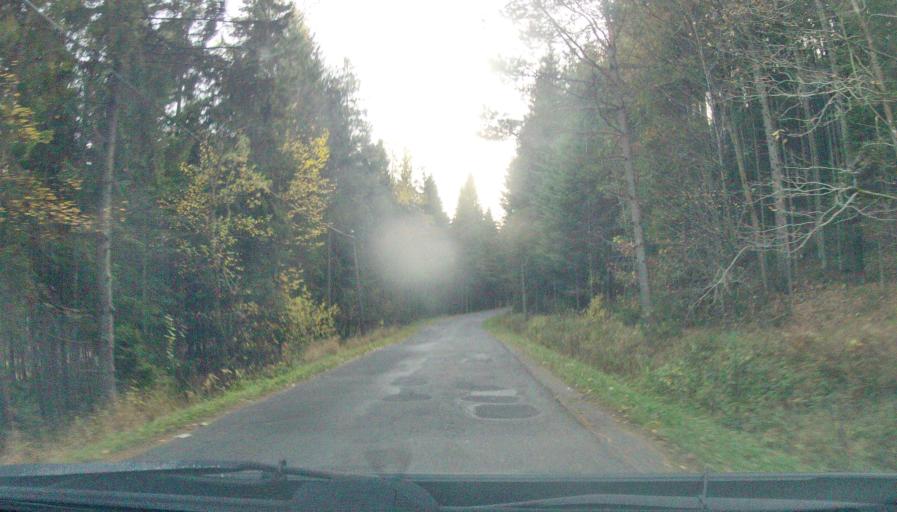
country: PL
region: Lesser Poland Voivodeship
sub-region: Powiat suski
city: Krzeszow
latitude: 49.7581
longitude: 19.4592
